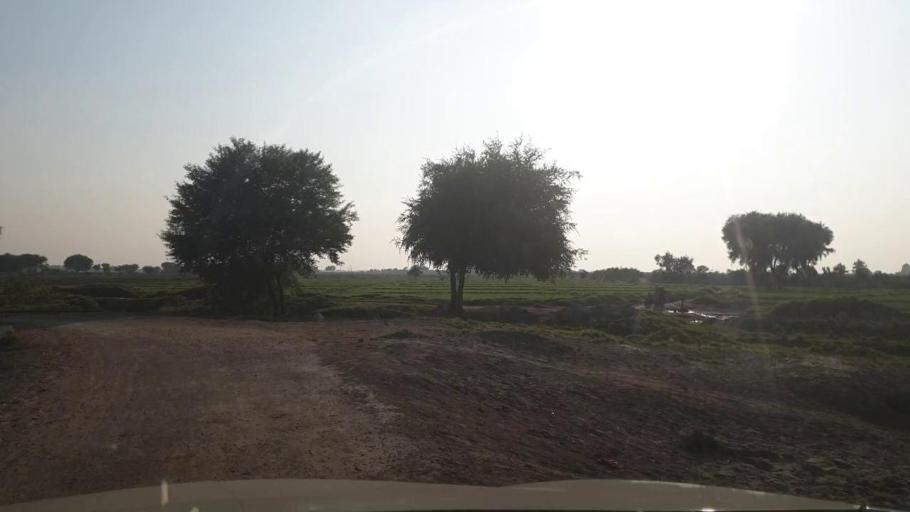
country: PK
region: Sindh
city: Bhan
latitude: 26.4636
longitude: 67.7211
